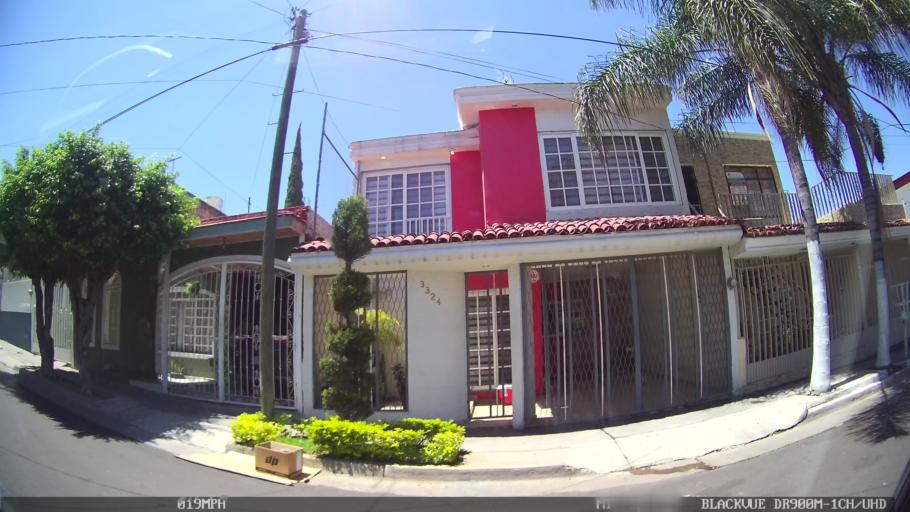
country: MX
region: Jalisco
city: Tlaquepaque
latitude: 20.6821
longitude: -103.2867
